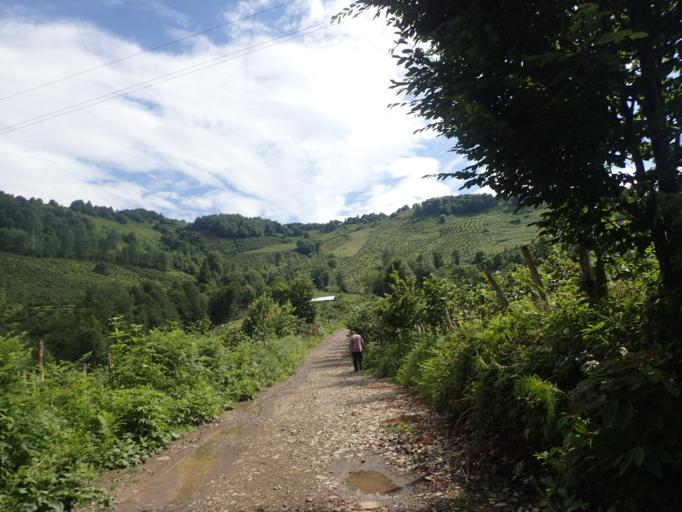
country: TR
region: Ordu
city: Akkus
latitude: 40.8941
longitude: 36.9859
